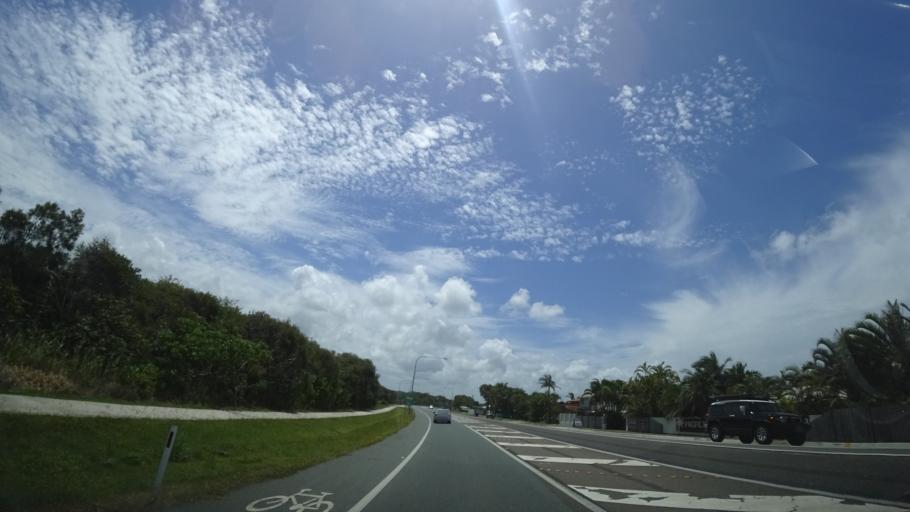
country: AU
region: Queensland
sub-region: Sunshine Coast
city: Coolum Beach
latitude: -26.5897
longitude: 153.0960
